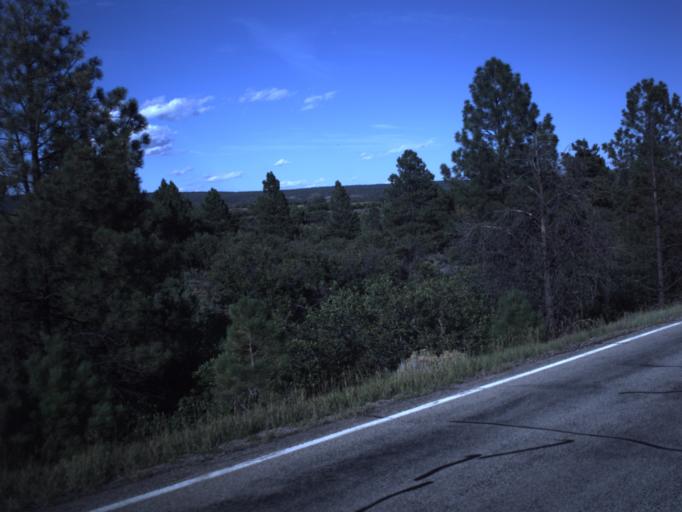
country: US
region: Utah
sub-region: Grand County
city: Moab
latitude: 38.3442
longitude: -109.1981
